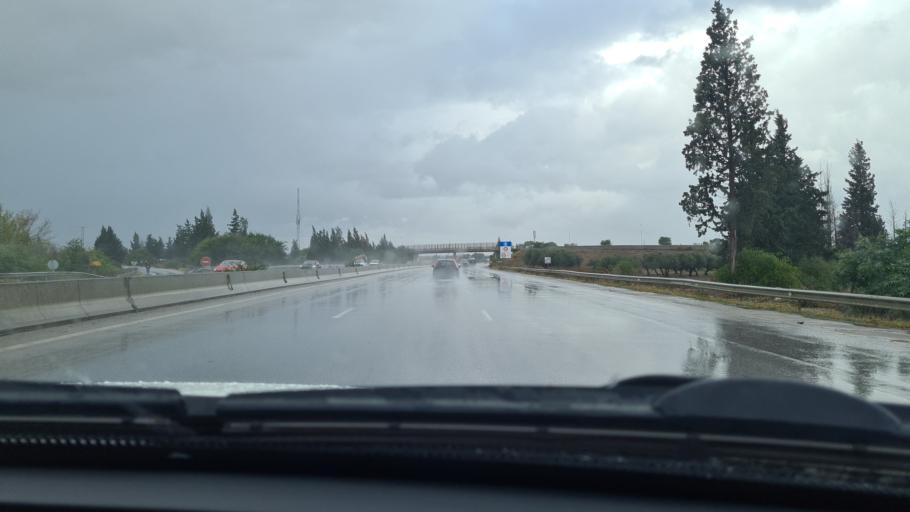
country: TN
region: Tunis
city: La Sebala du Mornag
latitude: 36.7160
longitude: 10.2716
